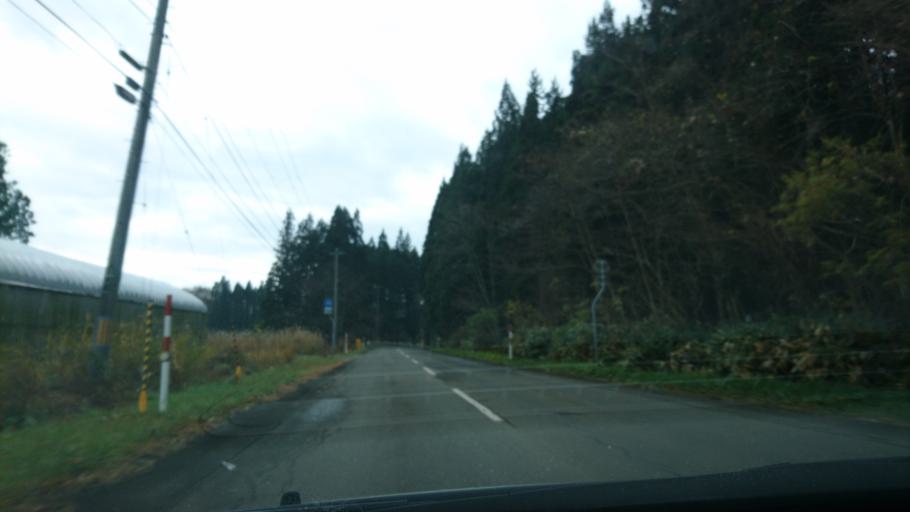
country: JP
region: Iwate
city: Ichinoseki
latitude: 38.9499
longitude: 140.9284
